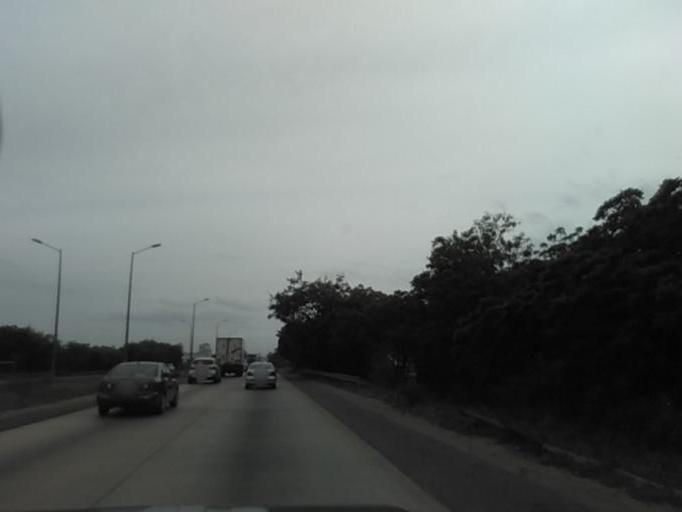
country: GH
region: Greater Accra
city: Medina Estates
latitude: 5.6295
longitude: -0.1569
